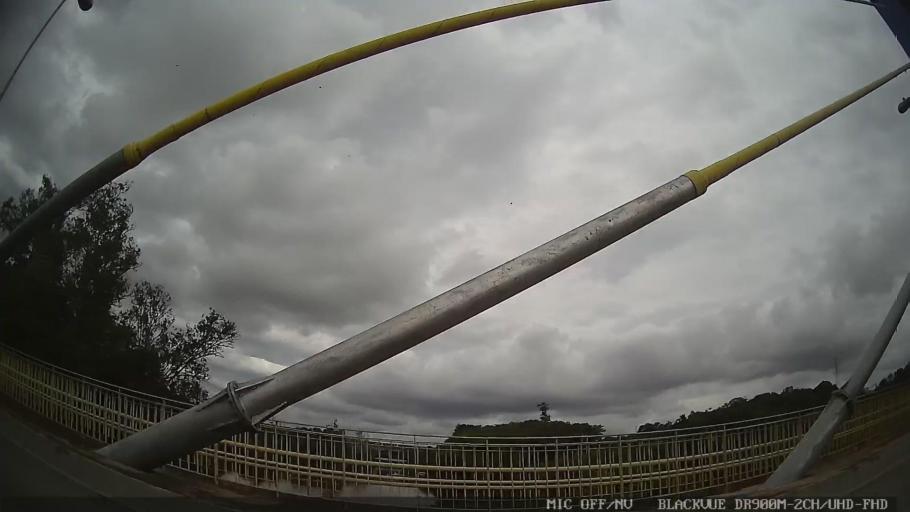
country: BR
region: Sao Paulo
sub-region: Salto
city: Salto
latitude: -23.2104
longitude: -47.2934
